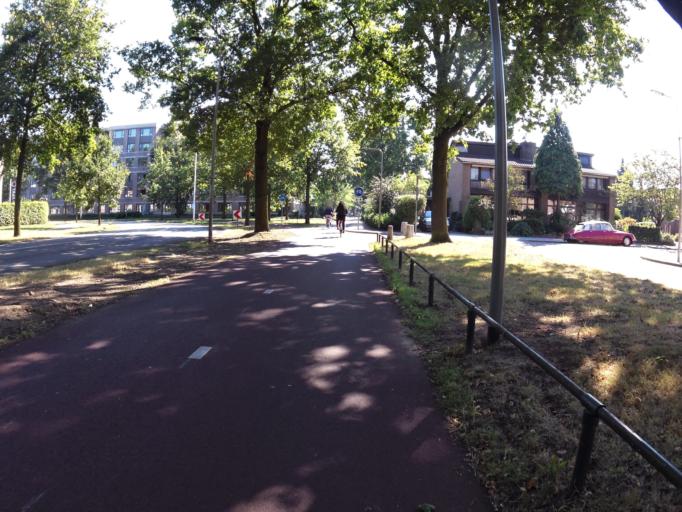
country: NL
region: North Brabant
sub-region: Gemeente Oss
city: Oss
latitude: 51.7565
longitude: 5.5090
